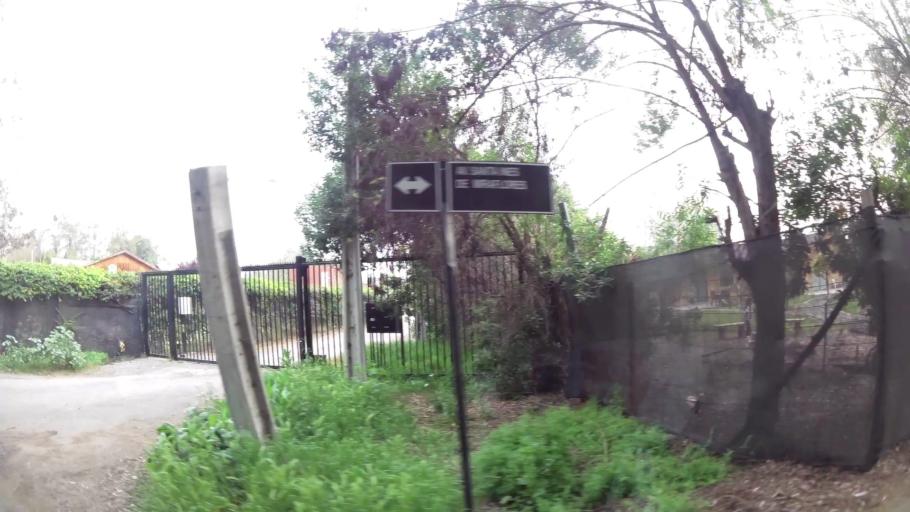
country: CL
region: Santiago Metropolitan
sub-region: Provincia de Chacabuco
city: Chicureo Abajo
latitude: -33.2694
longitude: -70.7021
